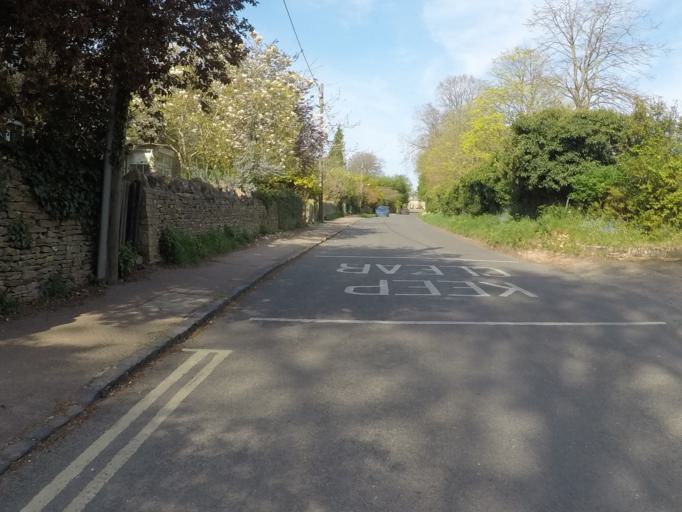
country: GB
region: England
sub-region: Oxfordshire
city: Charlbury
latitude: 51.8743
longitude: -1.4804
